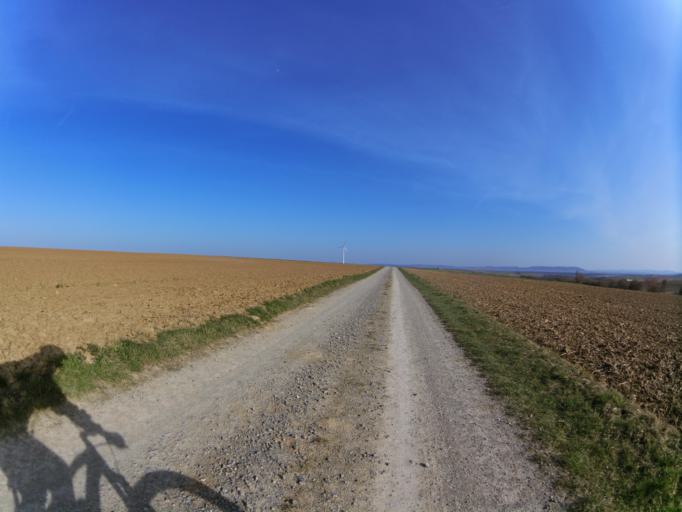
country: DE
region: Bavaria
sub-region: Regierungsbezirk Unterfranken
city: Prosselsheim
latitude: 49.8355
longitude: 10.1272
